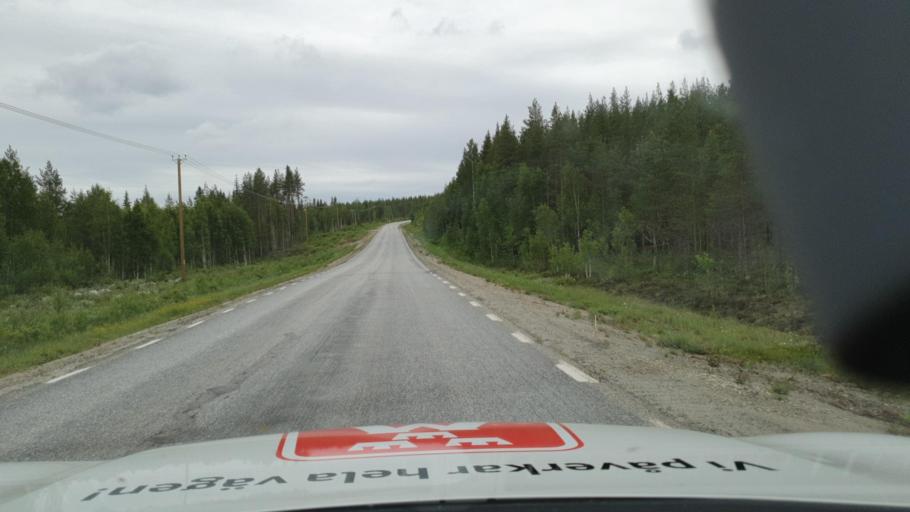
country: SE
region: Vaesterbotten
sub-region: Lycksele Kommun
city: Lycksele
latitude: 64.1548
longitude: 18.3577
